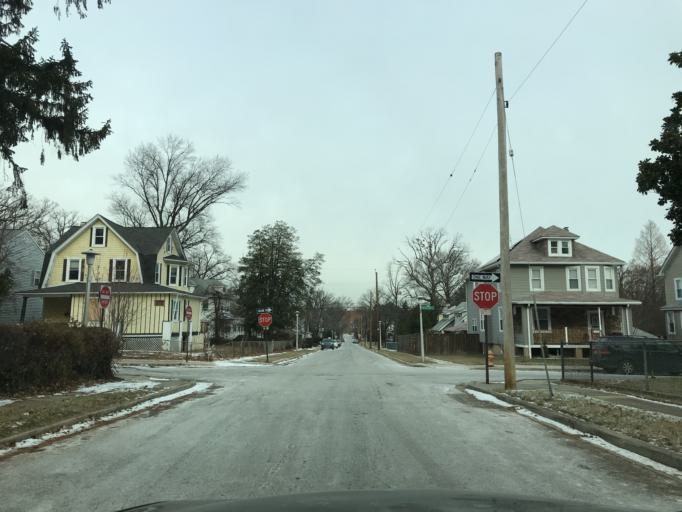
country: US
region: Maryland
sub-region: Baltimore County
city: Towson
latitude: 39.3504
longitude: -76.6017
